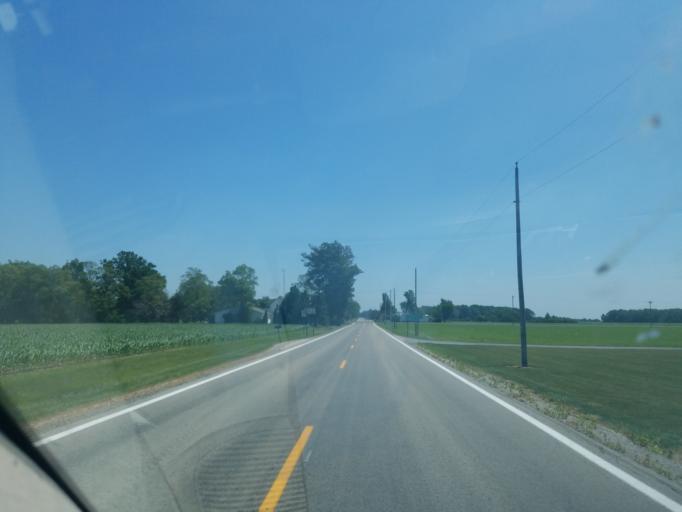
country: US
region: Ohio
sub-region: Allen County
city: Spencerville
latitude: 40.7430
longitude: -84.4188
